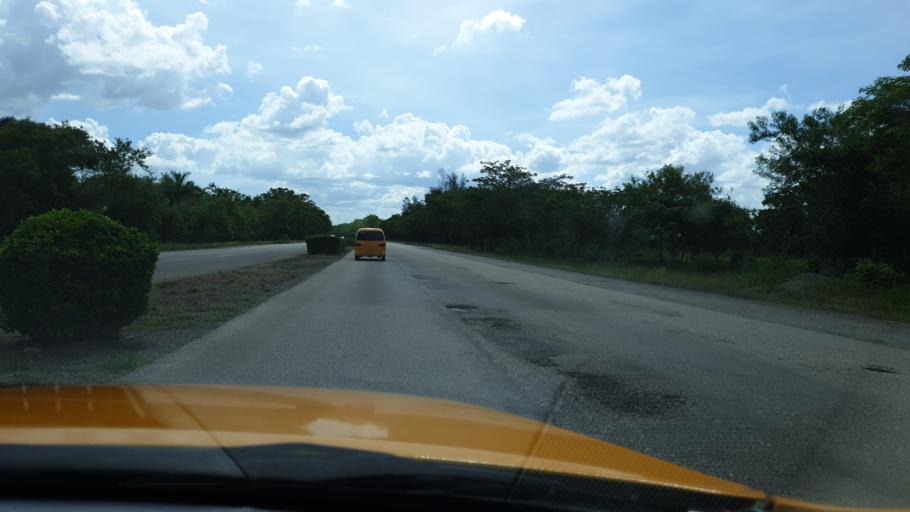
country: CU
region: Cienfuegos
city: Cruces
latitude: 22.4548
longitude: -80.3031
